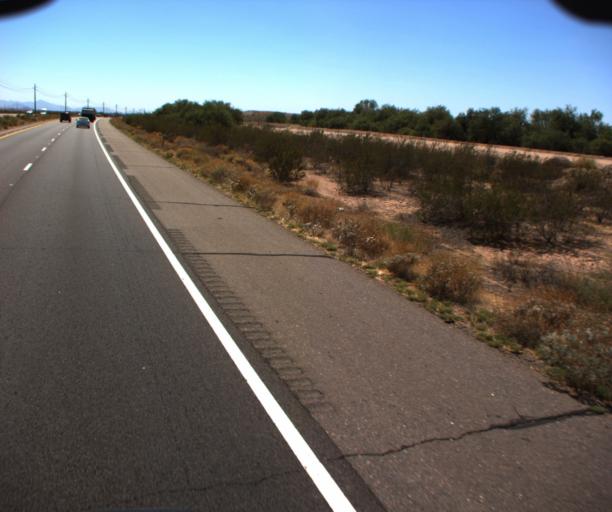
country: US
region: Arizona
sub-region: Maricopa County
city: Mesa
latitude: 33.5108
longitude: -111.7624
